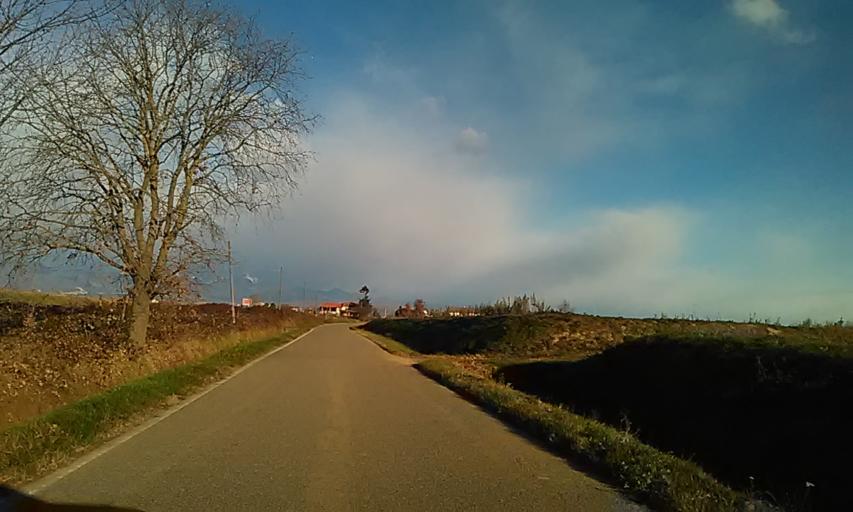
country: IT
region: Piedmont
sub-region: Provincia di Vercelli
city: Buronzo
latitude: 45.4868
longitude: 8.2718
